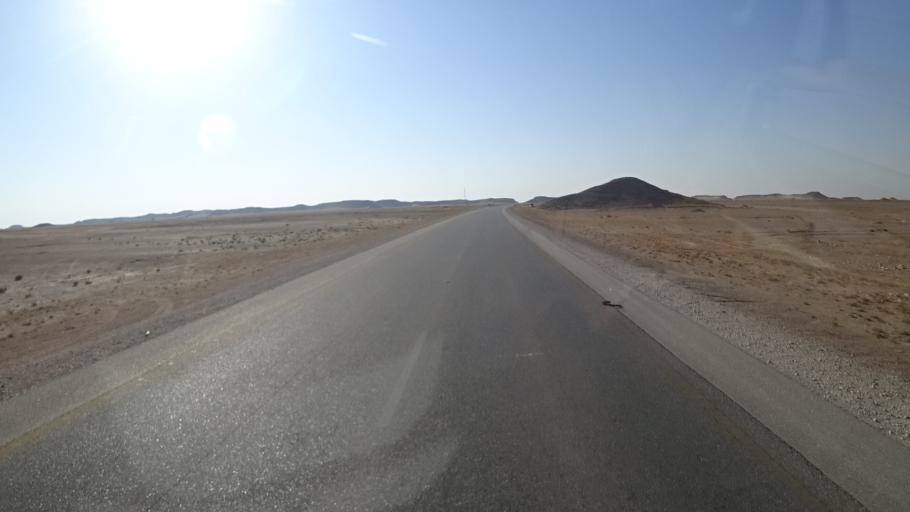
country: OM
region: Zufar
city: Salalah
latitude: 17.6394
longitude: 53.8730
